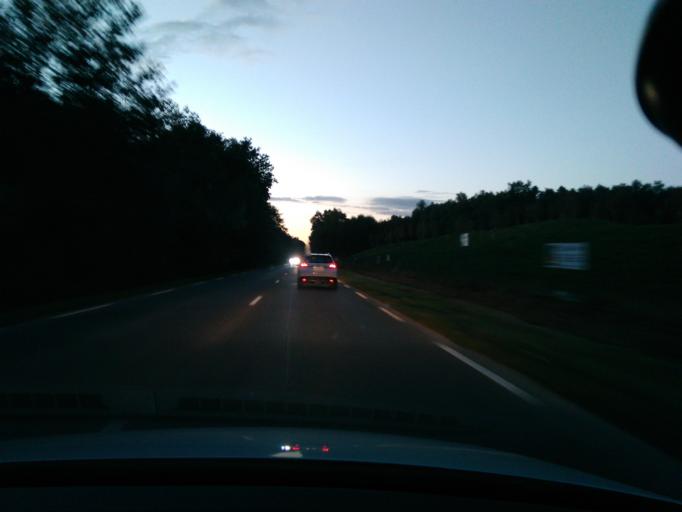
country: FR
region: Ile-de-France
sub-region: Departement de Seine-et-Marne
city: Villeneuve-le-Comte
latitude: 48.8241
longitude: 2.8101
